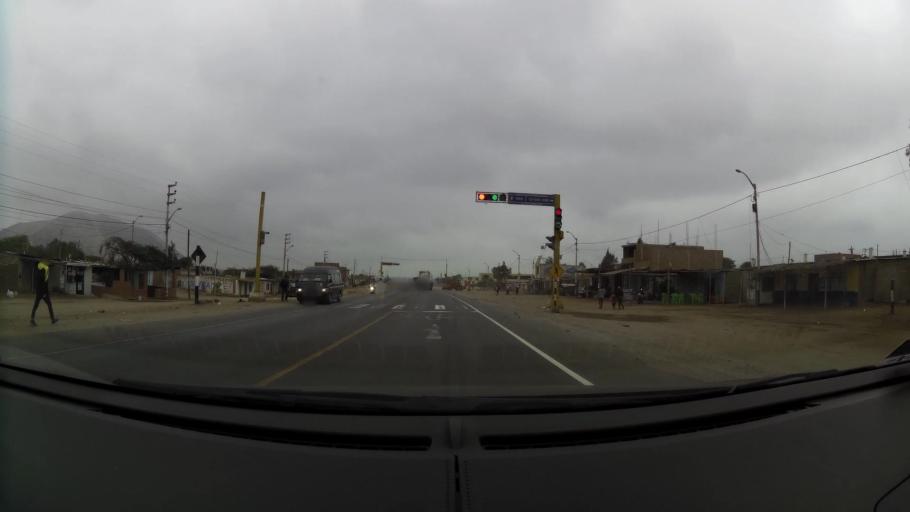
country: PE
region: La Libertad
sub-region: Viru
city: Viru
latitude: -8.4477
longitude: -78.7374
